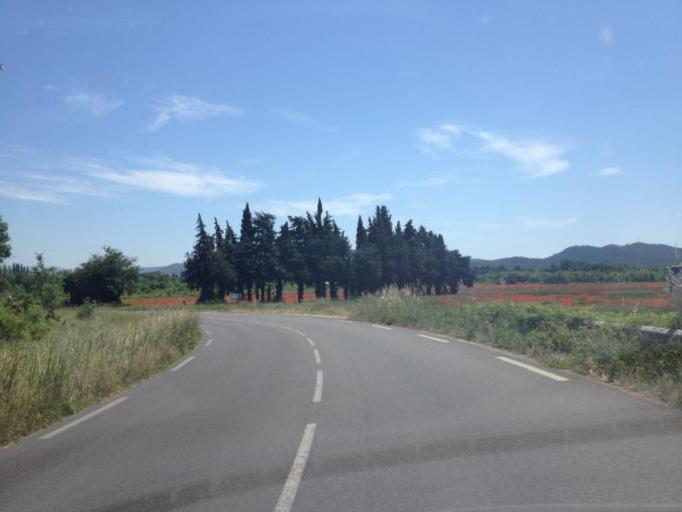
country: FR
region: Provence-Alpes-Cote d'Azur
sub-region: Departement du Vaucluse
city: Lauris
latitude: 43.7419
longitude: 5.3445
